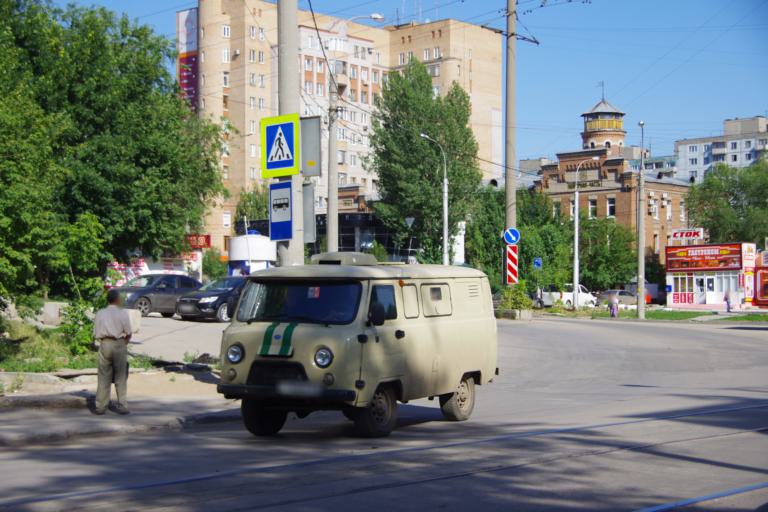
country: RU
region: Samara
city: Samara
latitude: 53.1976
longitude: 50.1400
